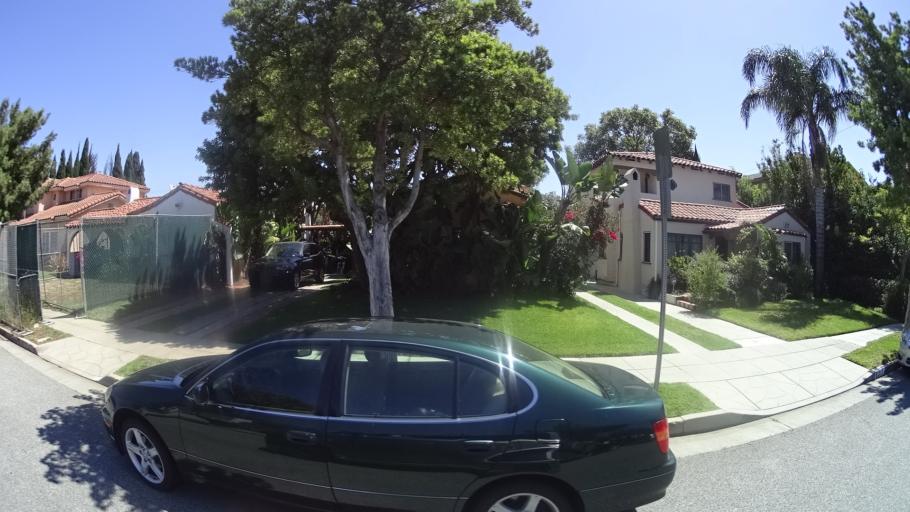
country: US
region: California
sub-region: Los Angeles County
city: Santa Monica
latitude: 34.0244
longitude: -118.4577
